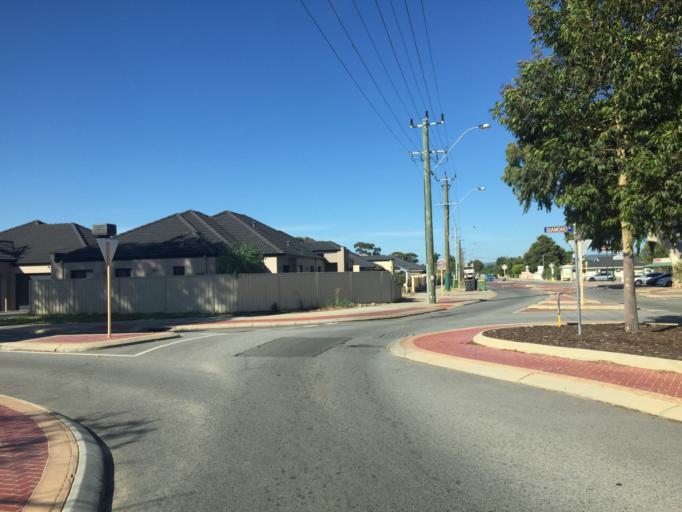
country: AU
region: Western Australia
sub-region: Canning
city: East Cannington
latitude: -32.0142
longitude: 115.9646
